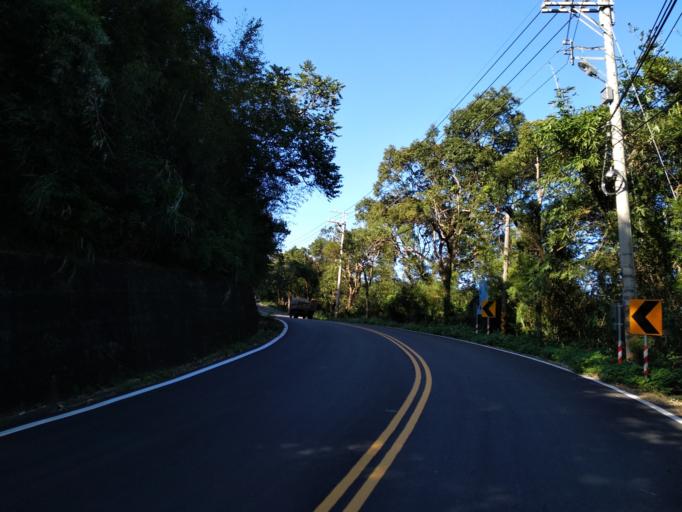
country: TW
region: Taiwan
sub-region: Hsinchu
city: Zhubei
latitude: 24.8595
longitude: 121.0956
